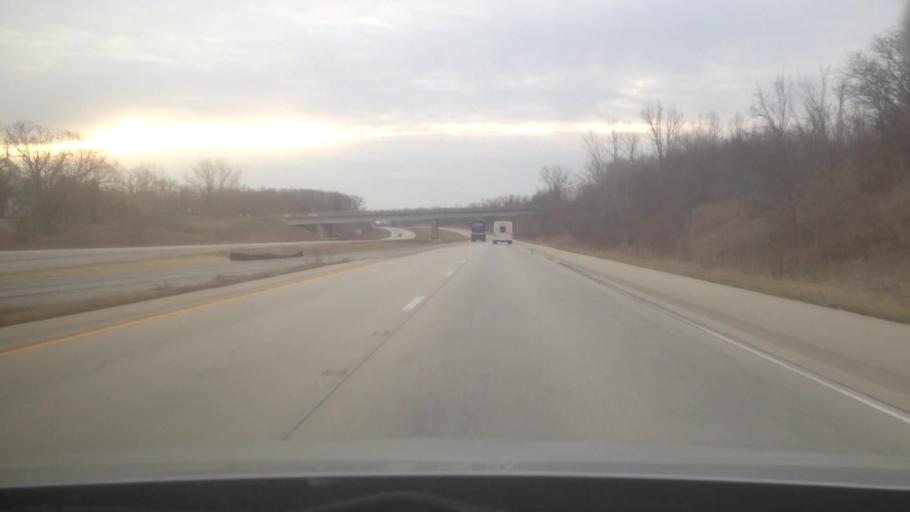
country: US
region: Illinois
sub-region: Macon County
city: Harristown
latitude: 39.8164
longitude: -89.0310
